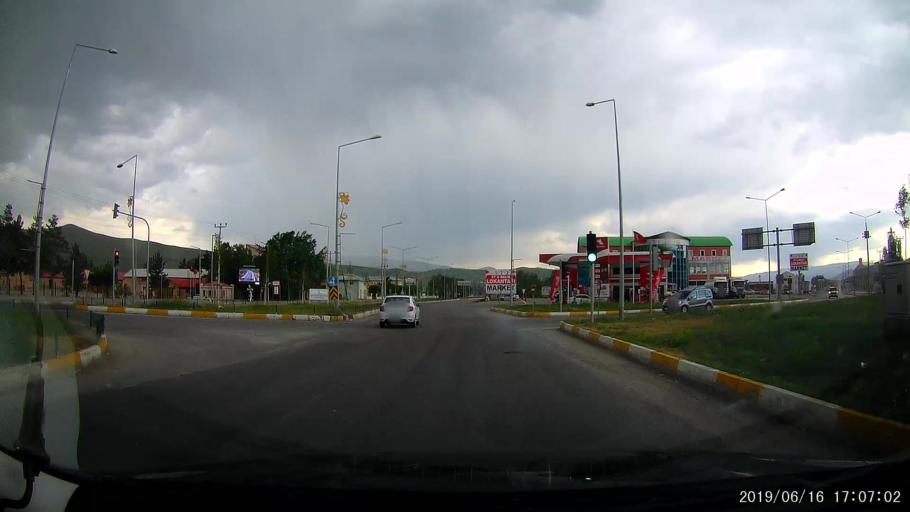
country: TR
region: Erzurum
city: Askale
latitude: 39.9187
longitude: 40.6827
